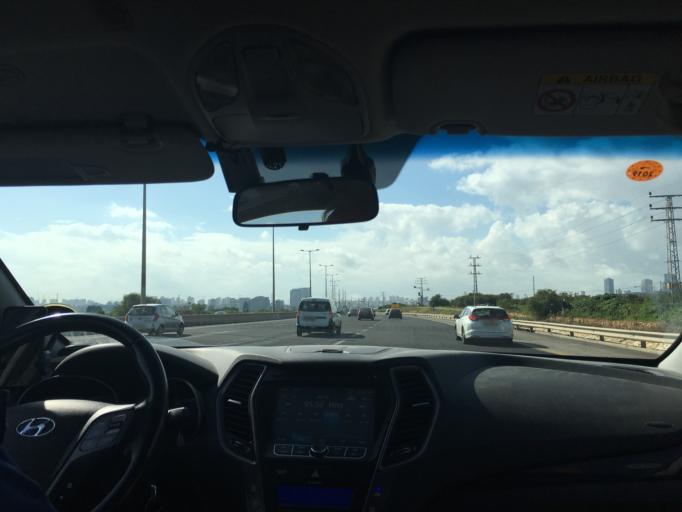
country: IL
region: Tel Aviv
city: Ramat HaSharon
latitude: 32.1205
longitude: 34.8526
